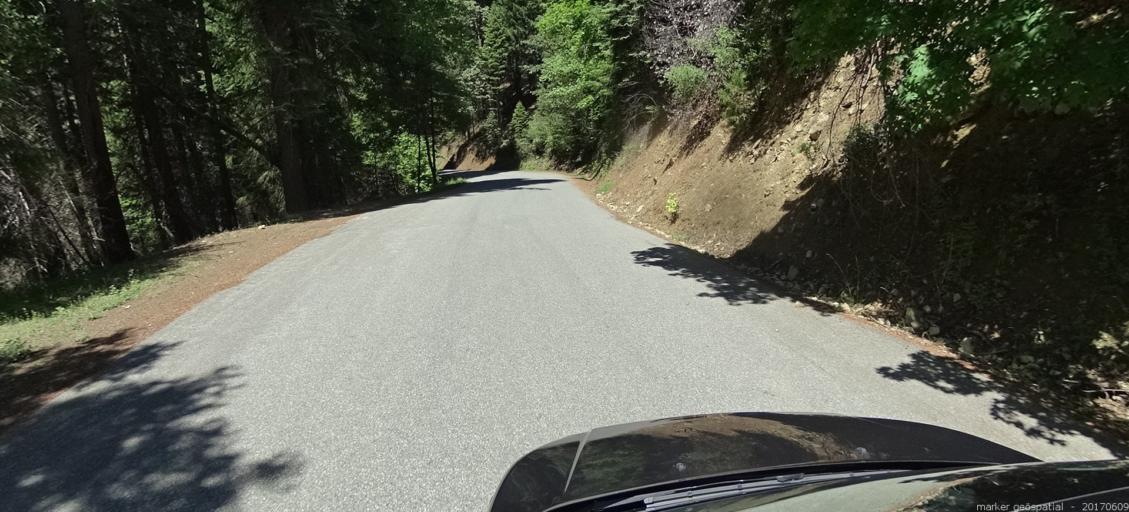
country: US
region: California
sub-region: Siskiyou County
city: Yreka
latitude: 41.3746
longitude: -123.0171
